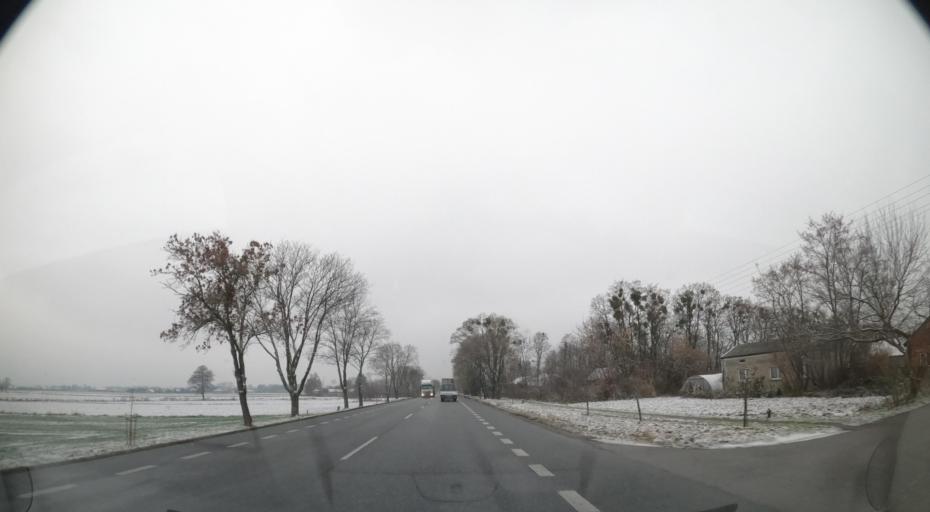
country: PL
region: Masovian Voivodeship
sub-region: Powiat sochaczewski
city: Paprotnia
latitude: 52.2071
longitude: 20.4832
